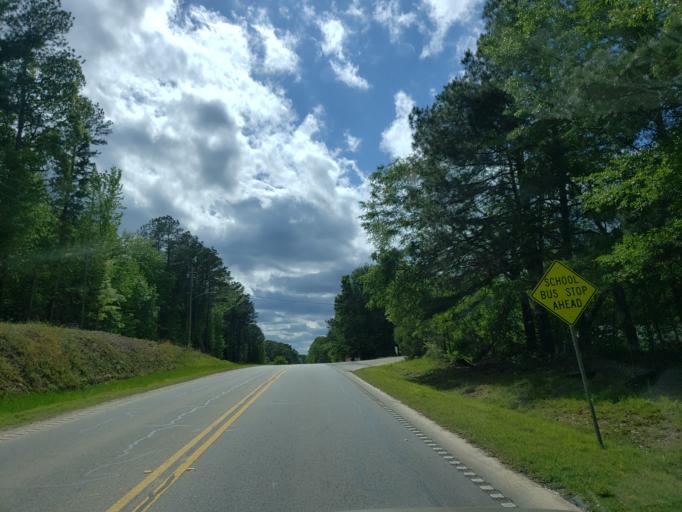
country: US
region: Georgia
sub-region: Haralson County
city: Tallapoosa
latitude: 33.7436
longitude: -85.3043
